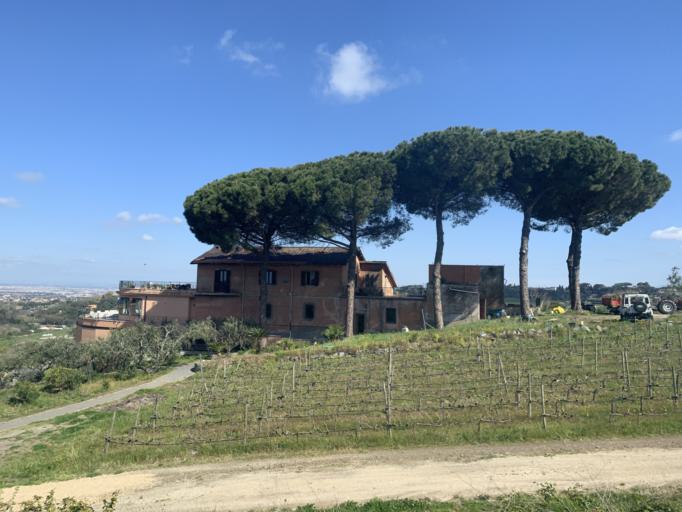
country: IT
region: Latium
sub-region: Citta metropolitana di Roma Capitale
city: Marino
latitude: 41.7852
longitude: 12.6461
